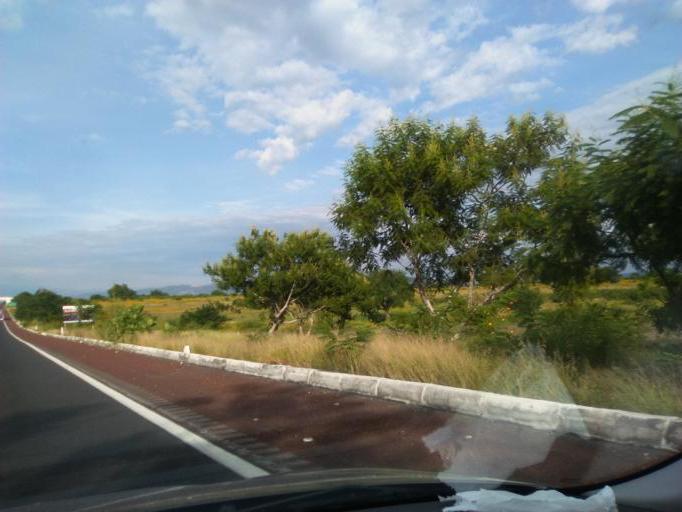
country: MX
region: Morelos
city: Xoxocotla
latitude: 18.7054
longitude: -99.2735
